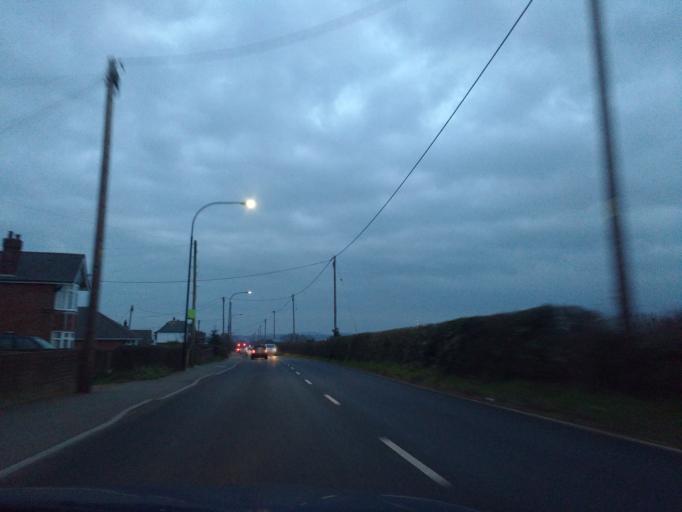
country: GB
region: England
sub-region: Isle of Wight
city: Northwood
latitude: 50.7277
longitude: -1.3057
